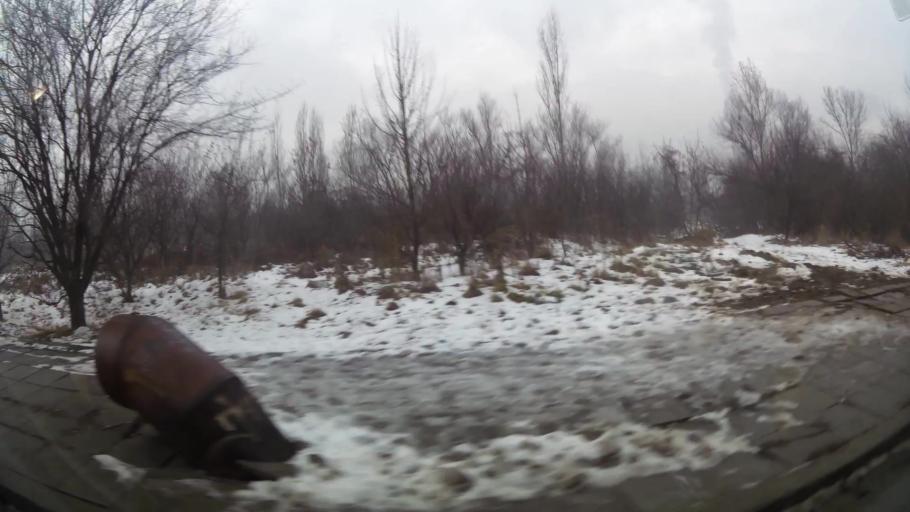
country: BG
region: Sofia-Capital
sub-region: Stolichna Obshtina
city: Sofia
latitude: 42.6861
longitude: 23.2637
